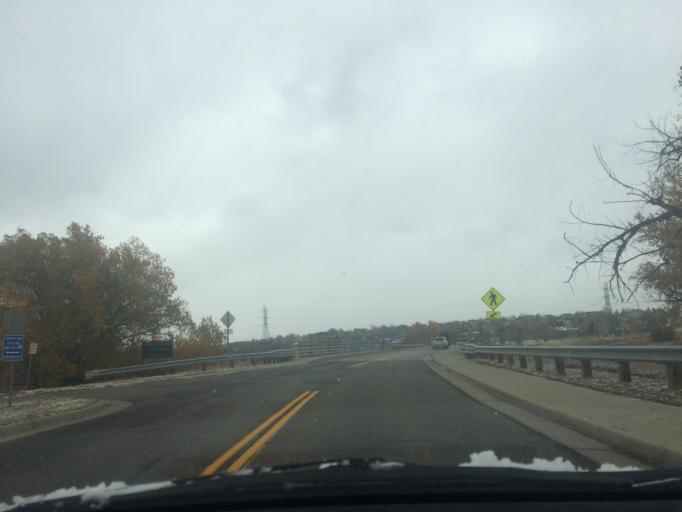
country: US
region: Colorado
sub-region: Boulder County
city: Erie
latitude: 40.0544
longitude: -105.0474
